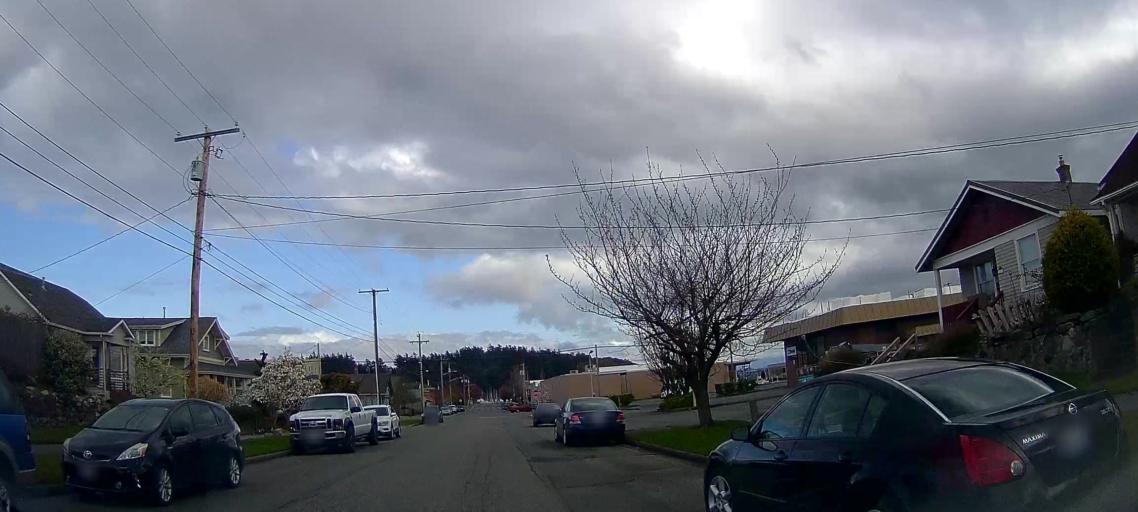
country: US
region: Washington
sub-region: Skagit County
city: Anacortes
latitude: 48.5152
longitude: -122.6155
